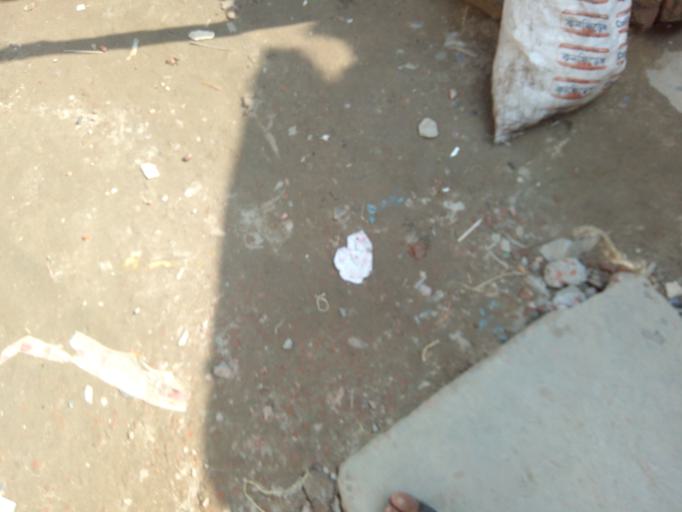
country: BD
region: Dhaka
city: Azimpur
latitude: 23.7096
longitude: 90.3792
